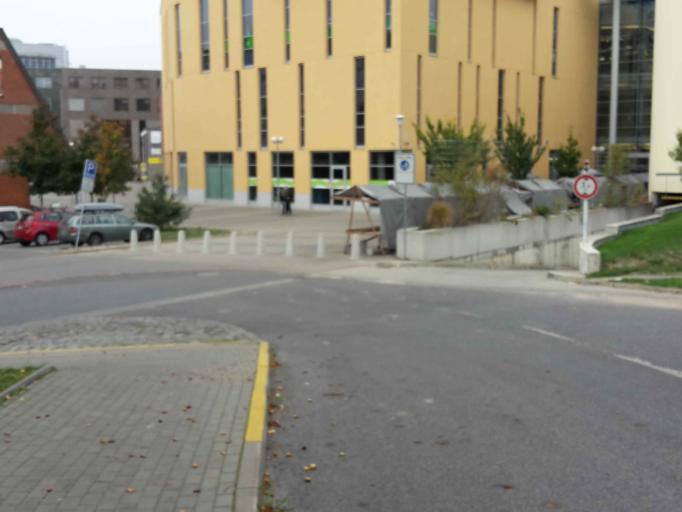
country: CZ
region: Liberecky
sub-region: Okres Liberec
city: Liberec
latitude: 50.7648
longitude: 15.0544
